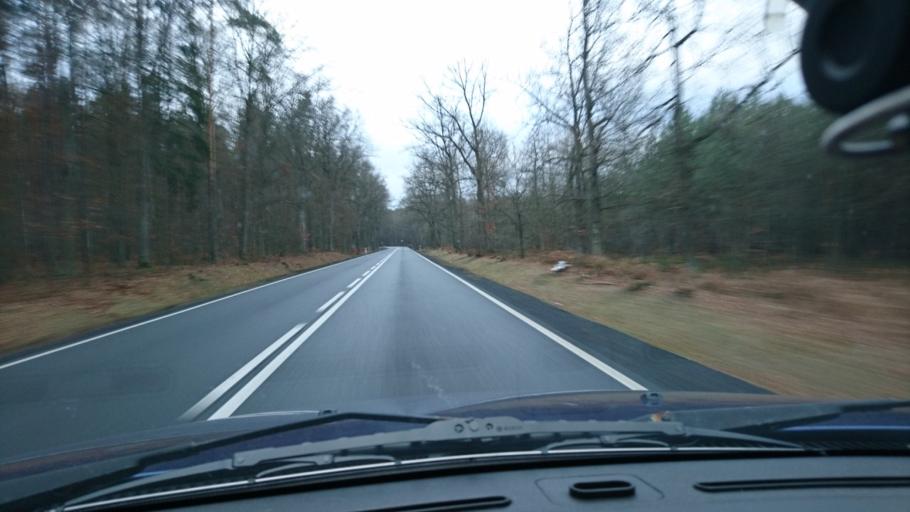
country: PL
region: Opole Voivodeship
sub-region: Powiat oleski
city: Olesno
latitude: 50.9345
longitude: 18.3315
